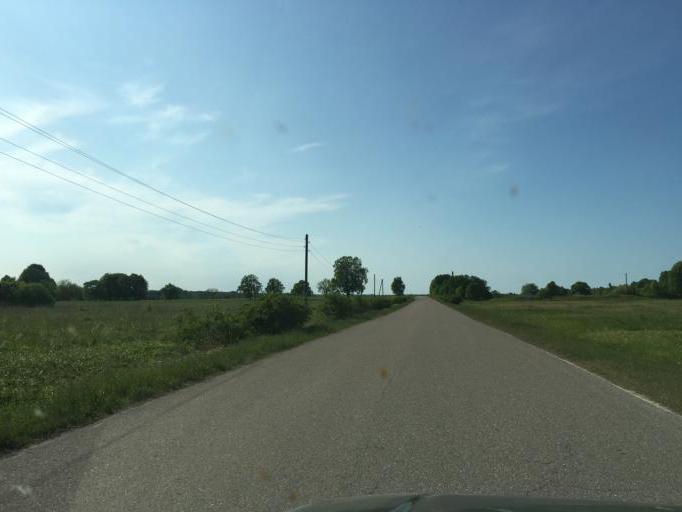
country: LV
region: Dundaga
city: Dundaga
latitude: 57.6087
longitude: 22.4449
